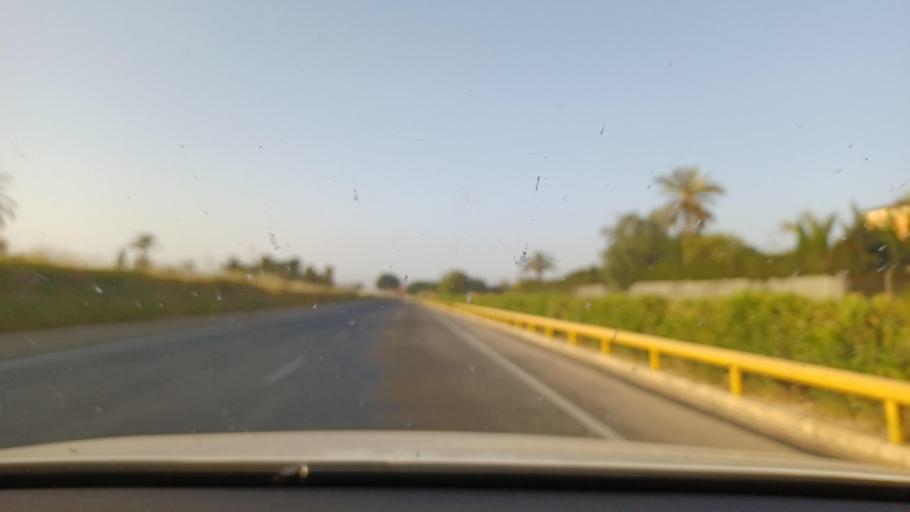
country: ES
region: Valencia
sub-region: Provincia de Alicante
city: Elche
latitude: 38.2190
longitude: -0.6972
